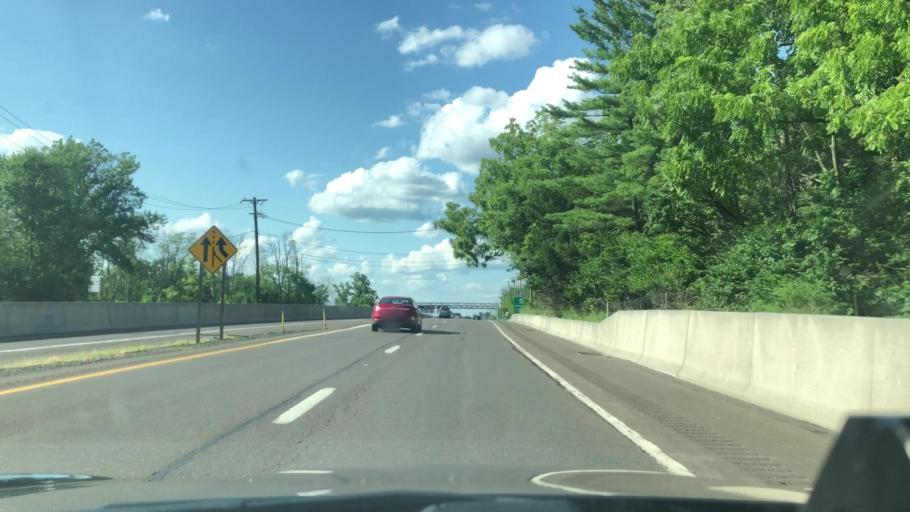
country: US
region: Pennsylvania
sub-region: Montgomery County
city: Spring House
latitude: 40.1980
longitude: -75.2238
